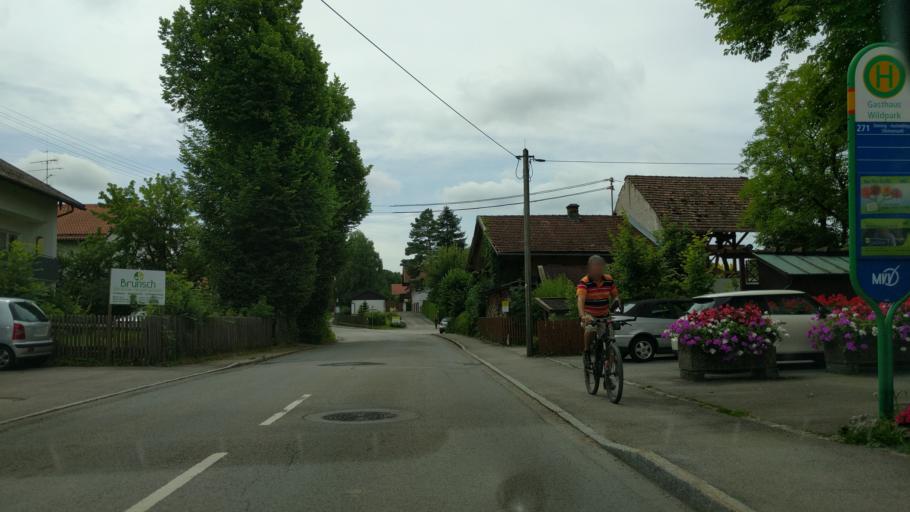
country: DE
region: Bavaria
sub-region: Upper Bavaria
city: Strasslach-Dingharting
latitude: 48.0033
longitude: 11.5142
